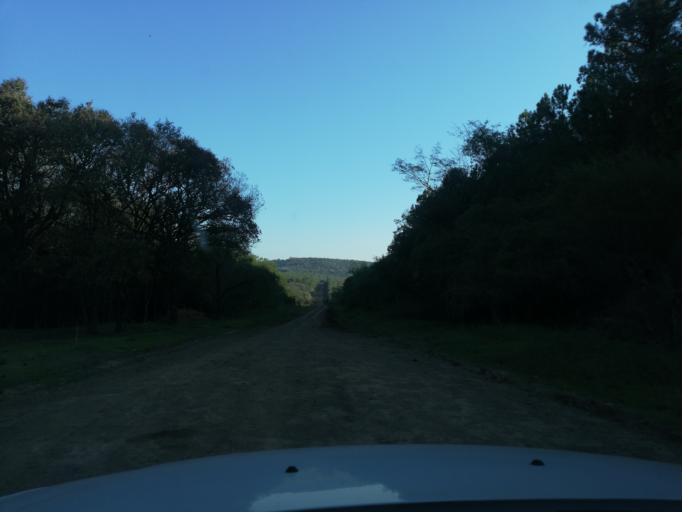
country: AR
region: Misiones
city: Cerro Cora
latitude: -27.5965
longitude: -55.6963
